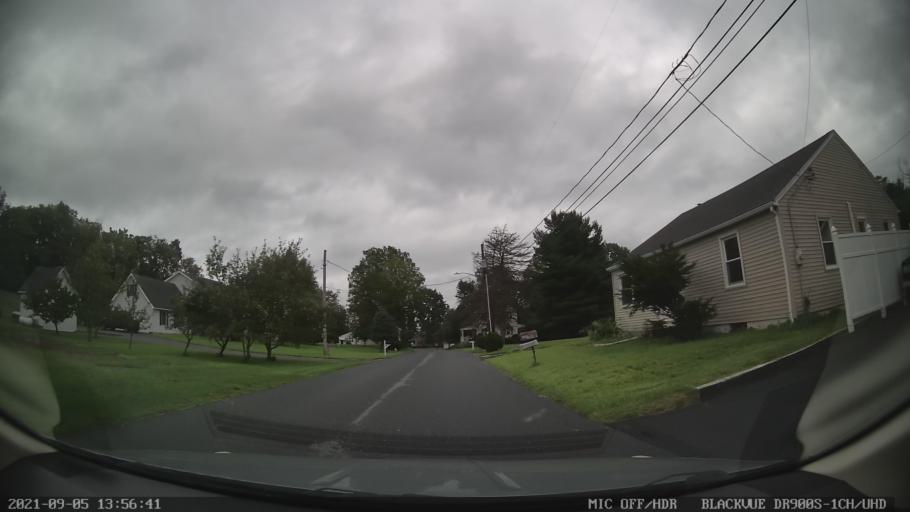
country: US
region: Pennsylvania
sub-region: Lehigh County
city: Stiles
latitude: 40.6578
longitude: -75.5195
